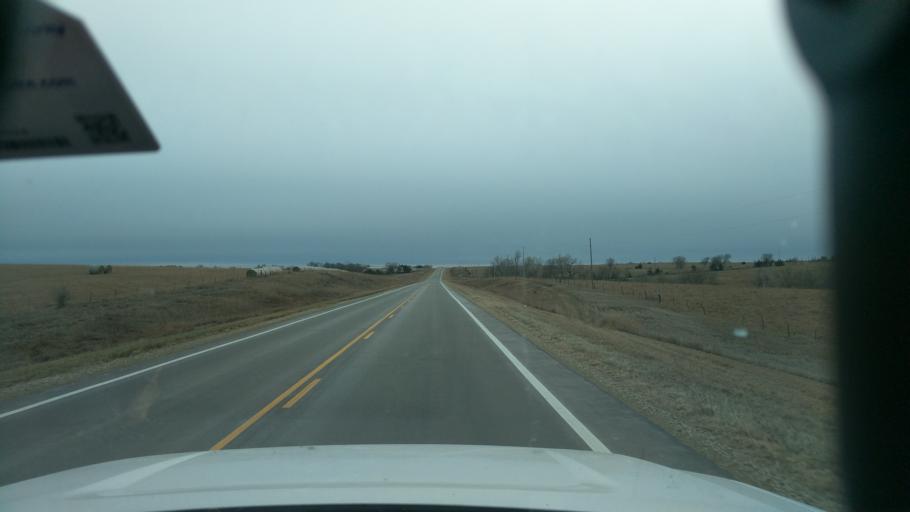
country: US
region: Kansas
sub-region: Dickinson County
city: Herington
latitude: 38.7576
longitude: -96.9274
